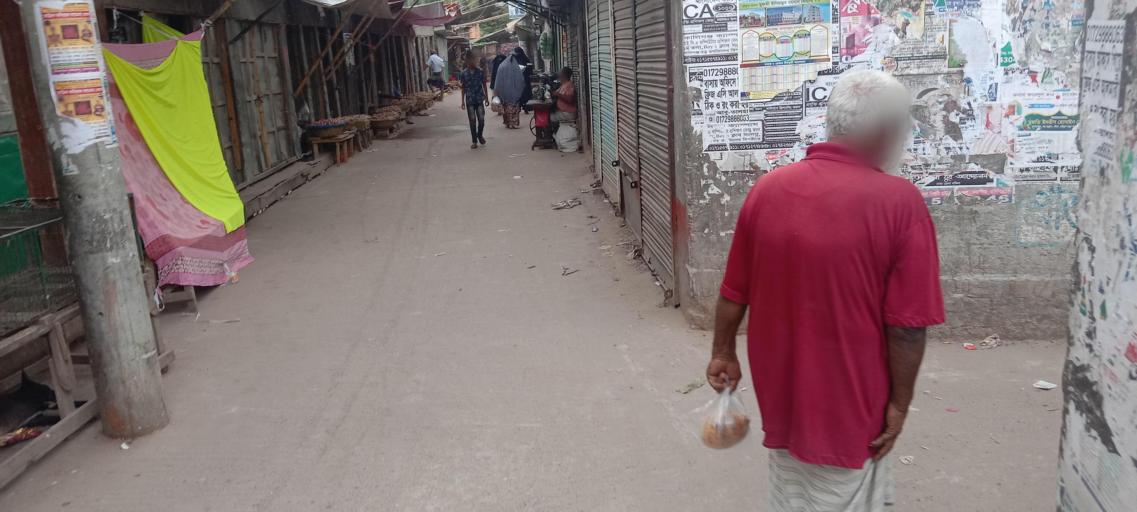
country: BD
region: Dhaka
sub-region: Dhaka
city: Dhaka
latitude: 23.6967
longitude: 90.3960
